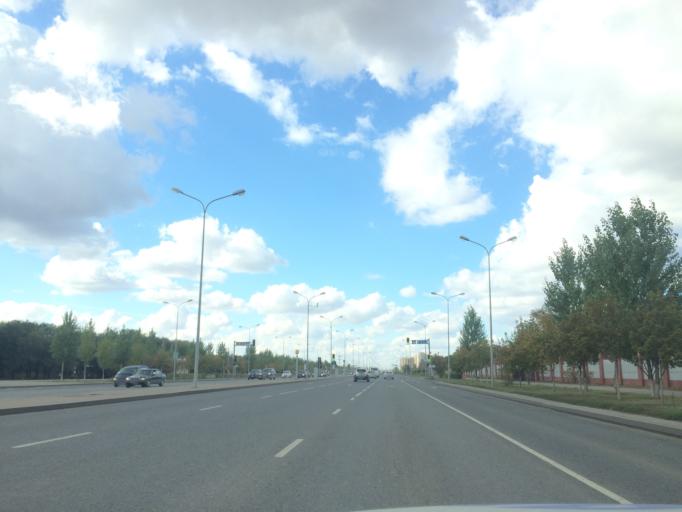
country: KZ
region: Astana Qalasy
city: Astana
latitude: 51.1850
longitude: 71.3603
